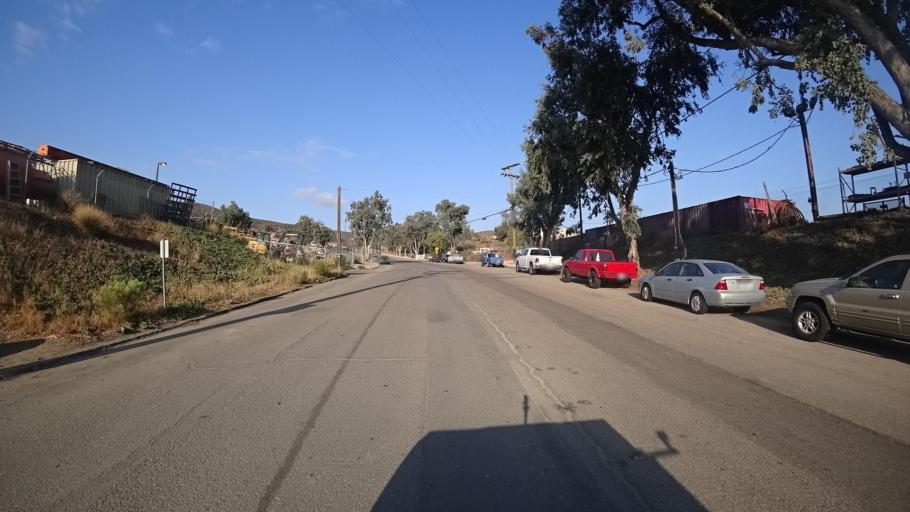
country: US
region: California
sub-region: San Diego County
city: Eucalyptus Hills
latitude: 32.9070
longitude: -116.9458
